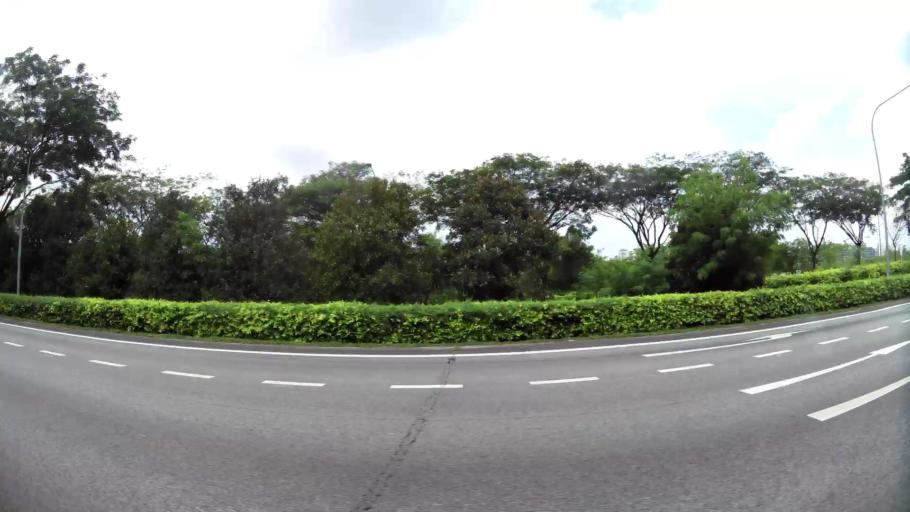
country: SG
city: Singapore
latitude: 1.3676
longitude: 103.9070
